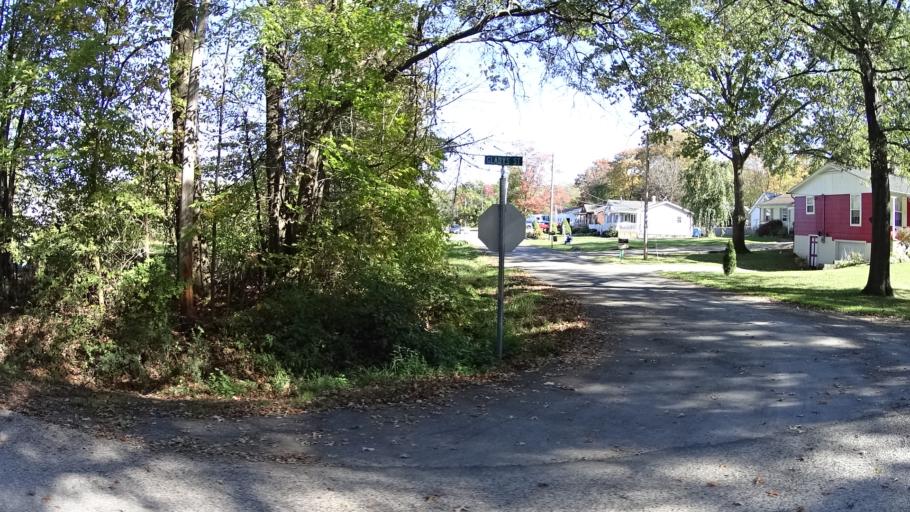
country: US
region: Ohio
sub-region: Lorain County
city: Sheffield
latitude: 41.4150
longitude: -82.1296
